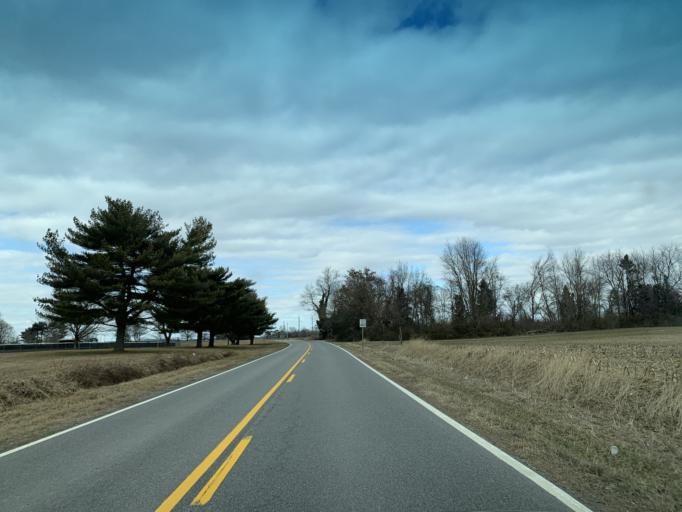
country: US
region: Maryland
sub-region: Queen Anne's County
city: Centreville
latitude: 38.9487
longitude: -76.0790
